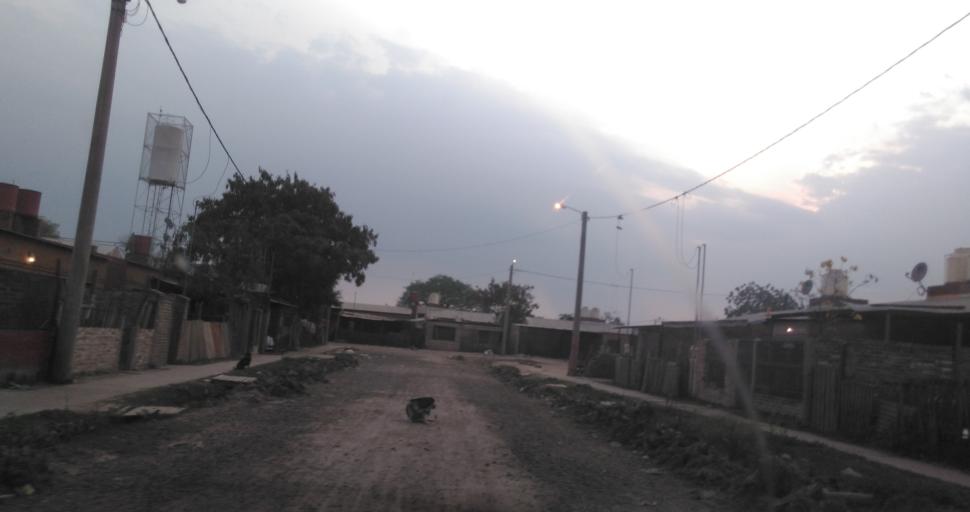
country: AR
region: Chaco
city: Fontana
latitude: -27.4319
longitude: -59.0063
